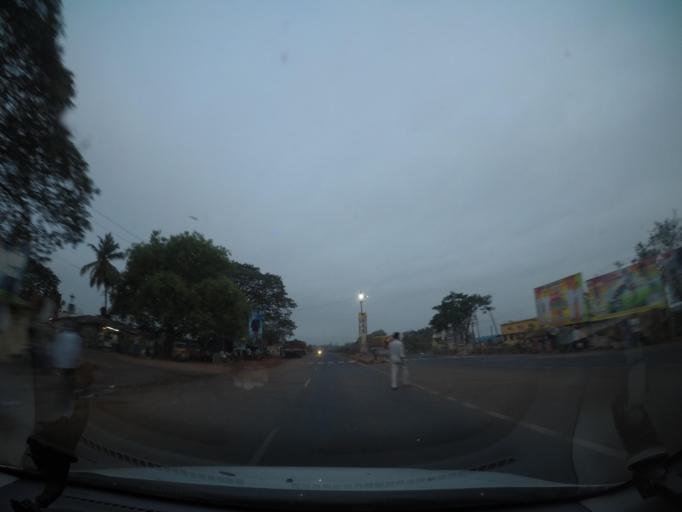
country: IN
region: Andhra Pradesh
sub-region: West Godavari
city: Tadepallegudem
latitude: 16.8093
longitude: 81.3239
